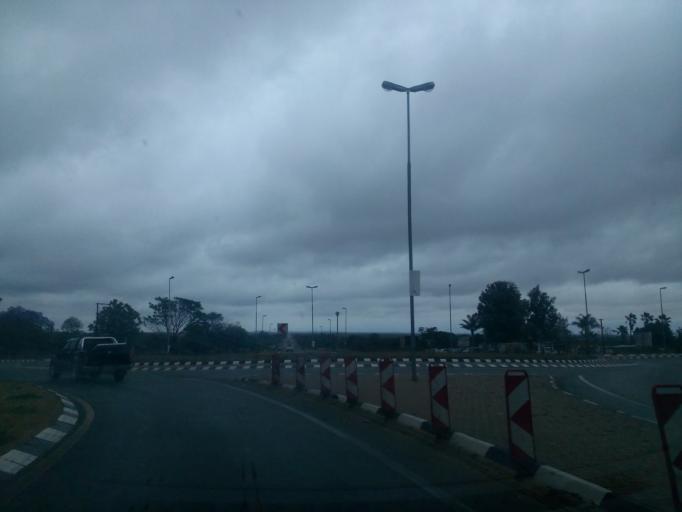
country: ZA
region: Limpopo
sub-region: Vhembe District Municipality
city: Louis Trichardt
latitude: -23.0779
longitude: 29.9089
